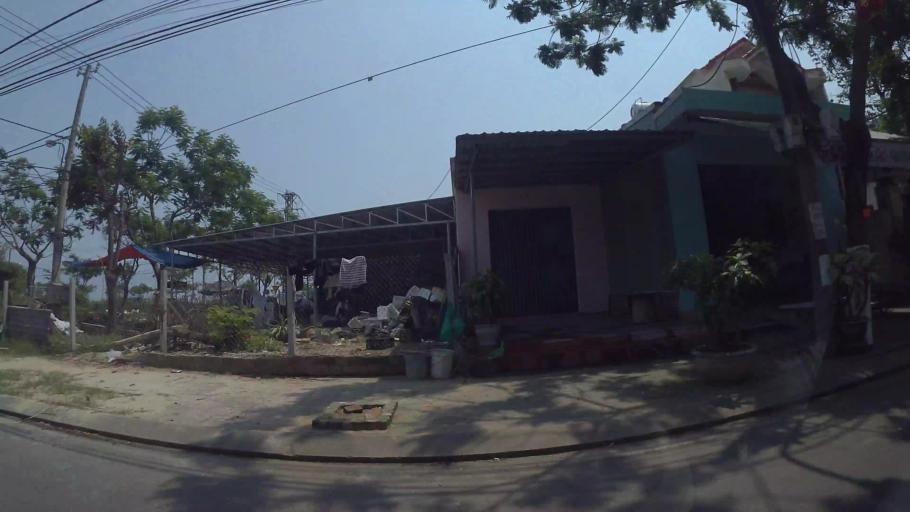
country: VN
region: Da Nang
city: Ngu Hanh Son
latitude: 15.9935
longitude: 108.2576
